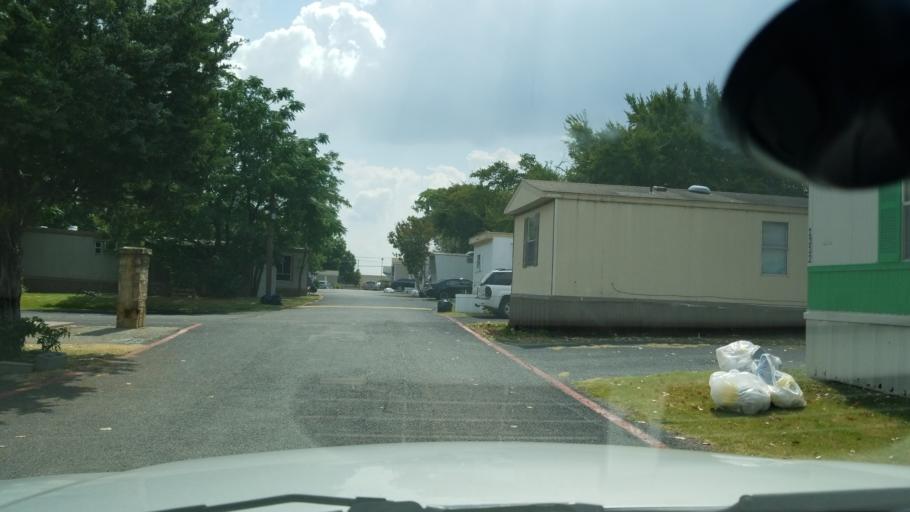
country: US
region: Texas
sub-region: Dallas County
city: Irving
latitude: 32.8323
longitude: -96.9092
